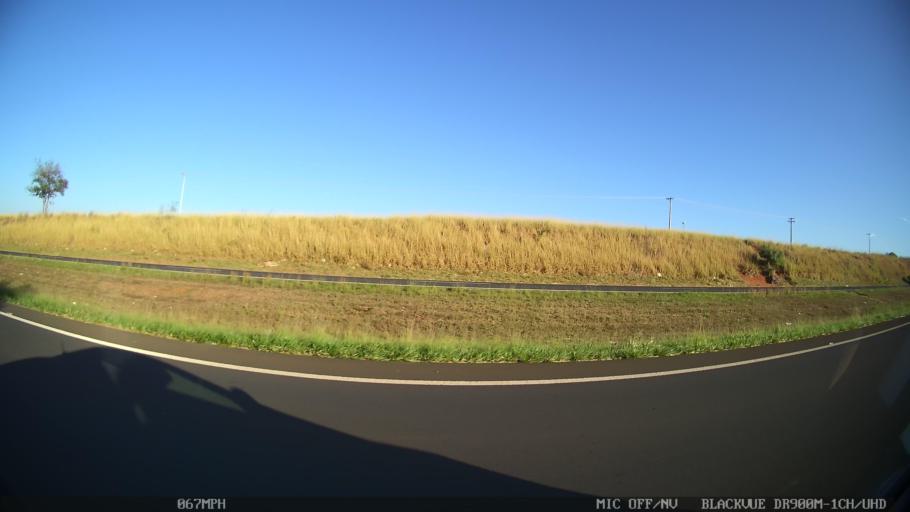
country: BR
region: Sao Paulo
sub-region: Sao Jose Do Rio Preto
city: Sao Jose do Rio Preto
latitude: -20.7985
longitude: -49.3291
